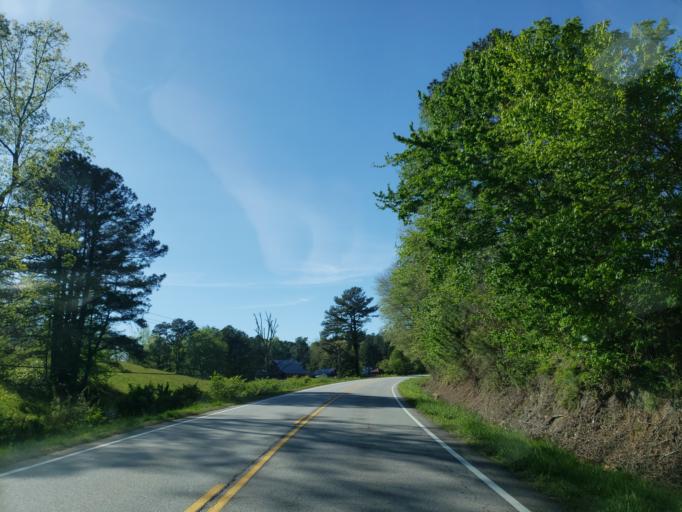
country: US
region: Georgia
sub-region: Haralson County
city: Tallapoosa
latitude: 33.8789
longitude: -85.3089
